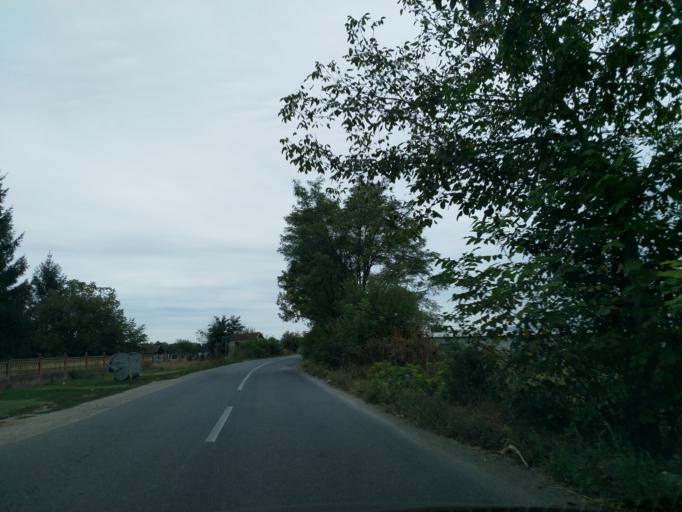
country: RS
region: Central Serbia
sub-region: Pomoravski Okrug
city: Paracin
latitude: 43.8335
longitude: 21.3654
